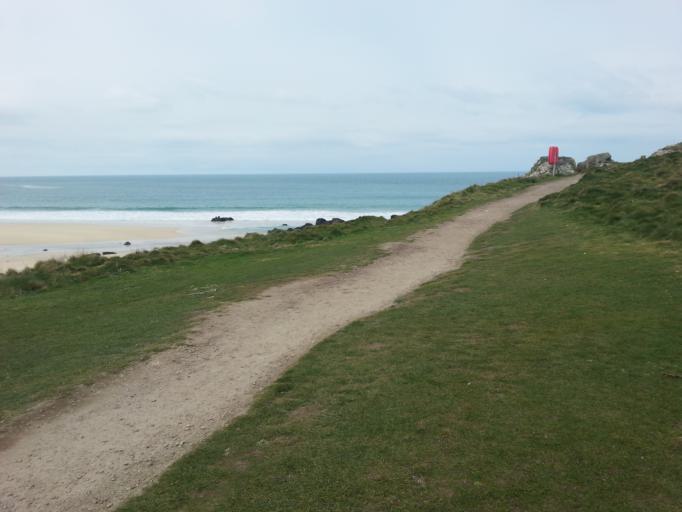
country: GB
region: England
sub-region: Cornwall
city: St Ives
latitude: 50.2173
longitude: -5.4792
